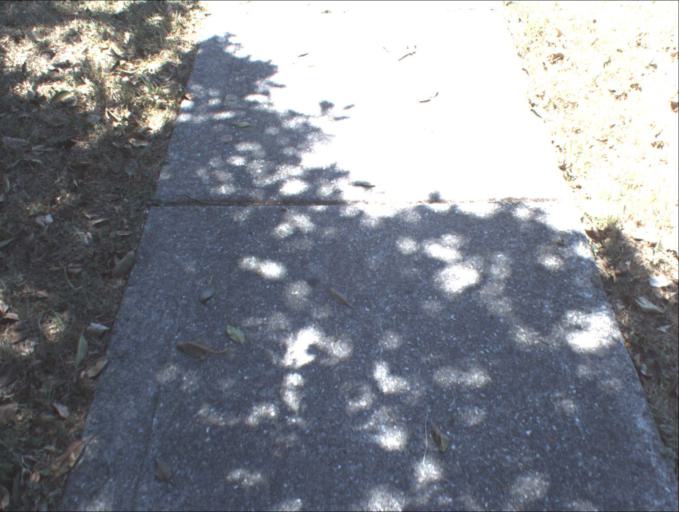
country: AU
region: Queensland
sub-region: Gold Coast
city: Yatala
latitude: -27.7135
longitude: 153.2104
